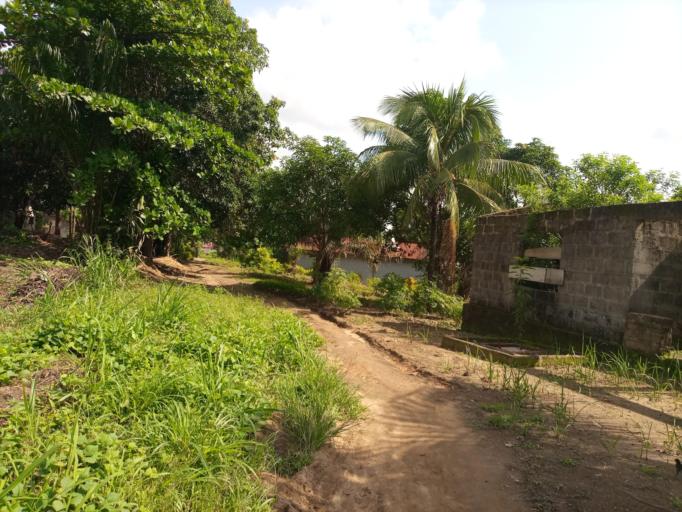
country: SL
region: Southern Province
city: Bo
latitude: 7.9668
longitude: -11.7654
